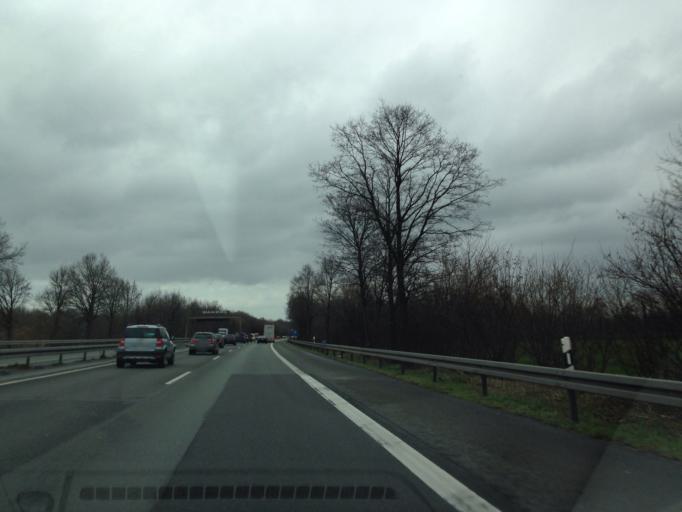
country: DE
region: North Rhine-Westphalia
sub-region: Regierungsbezirk Munster
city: Recklinghausen
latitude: 51.6285
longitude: 7.1667
